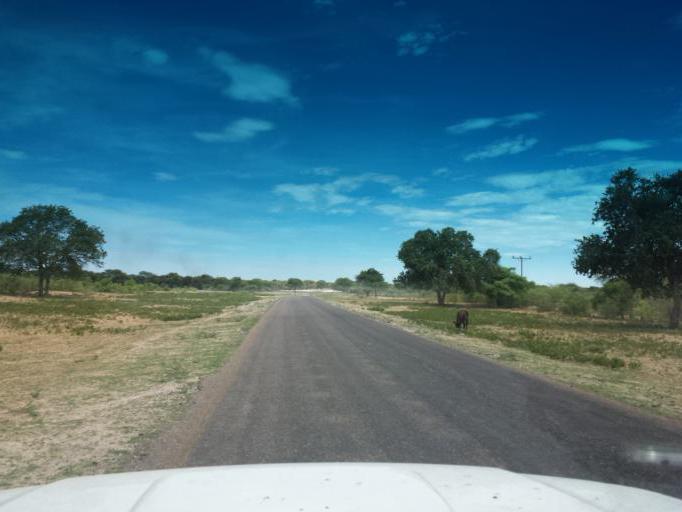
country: BW
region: North West
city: Shakawe
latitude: -18.7389
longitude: 22.1635
